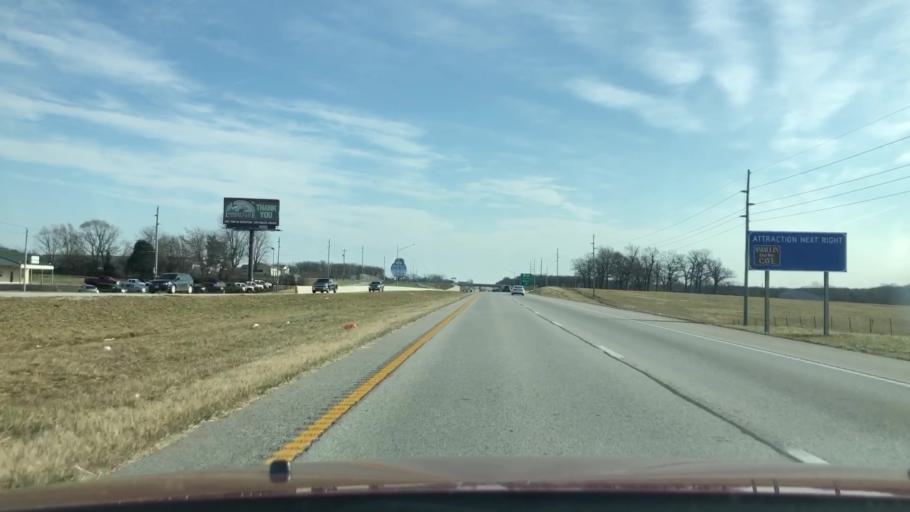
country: US
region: Missouri
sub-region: Christian County
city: Ozark
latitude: 37.1204
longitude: -93.1964
